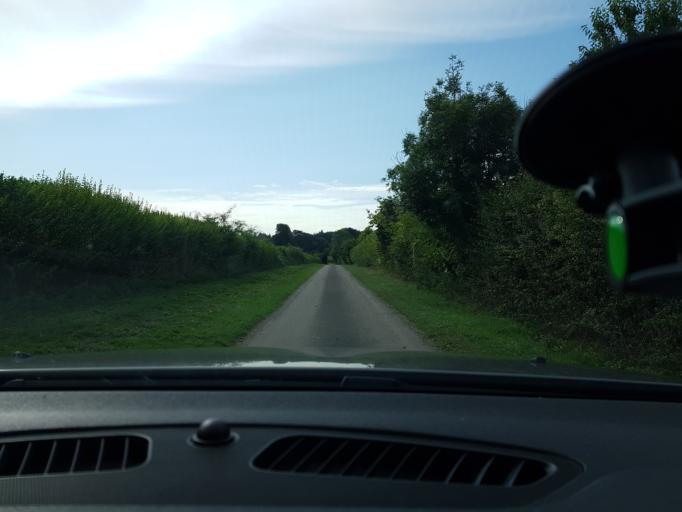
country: GB
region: England
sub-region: West Berkshire
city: Kintbury
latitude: 51.3995
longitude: -1.4836
